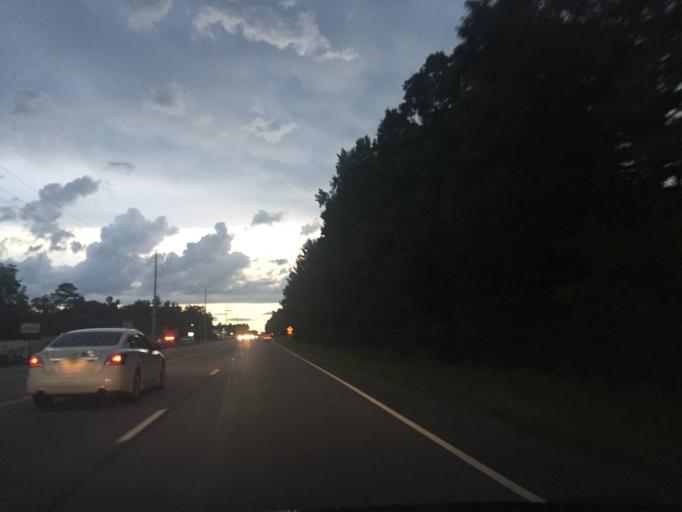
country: US
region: Georgia
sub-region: Liberty County
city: Hinesville
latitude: 31.8381
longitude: -81.5387
